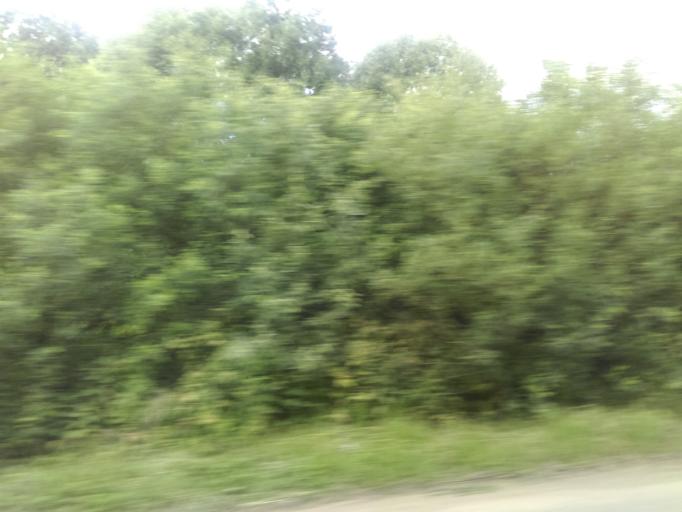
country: RU
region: Moskovskaya
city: Vostryakovo
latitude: 55.3887
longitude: 37.8088
